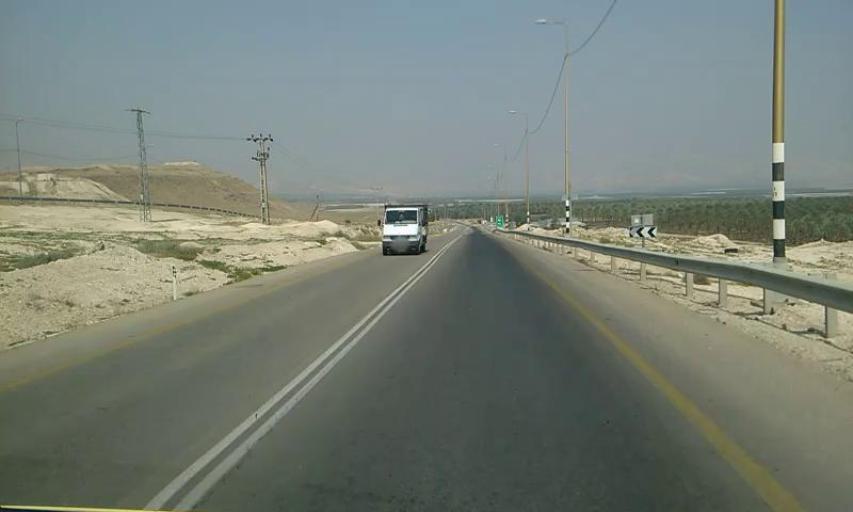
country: PS
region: West Bank
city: Al `Awja
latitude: 31.9721
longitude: 35.4700
